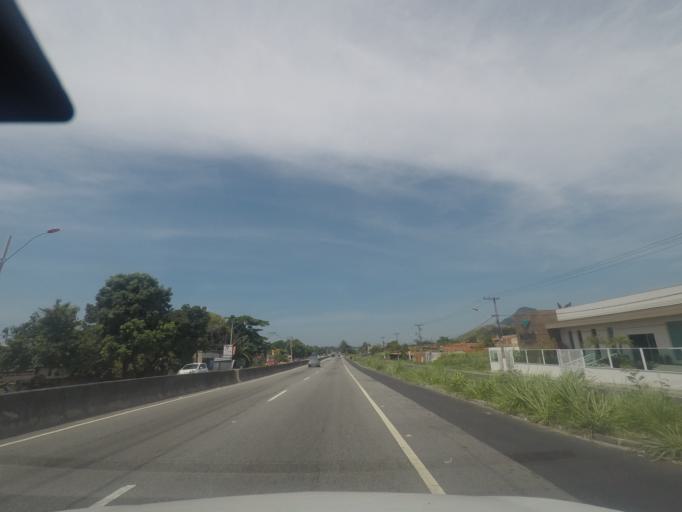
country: BR
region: Rio de Janeiro
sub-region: Marica
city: Marica
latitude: -22.9232
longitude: -42.8609
